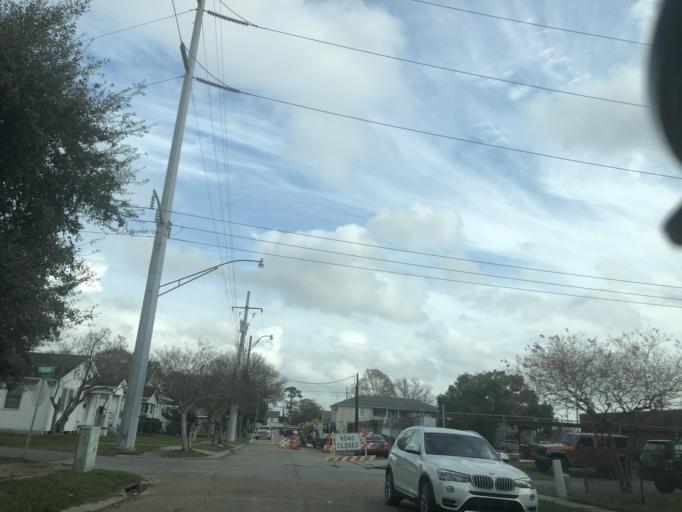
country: US
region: Louisiana
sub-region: Jefferson Parish
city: Metairie Terrace
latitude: 29.9767
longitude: -90.1620
